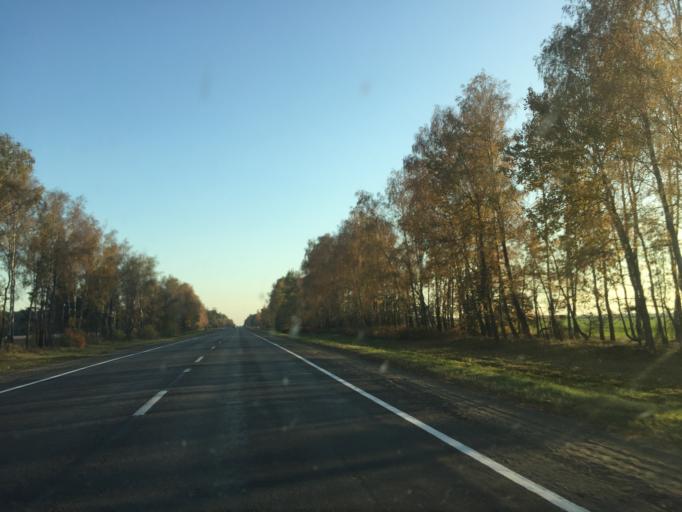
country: BY
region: Mogilev
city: Poselok Voskhod
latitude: 53.7370
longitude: 30.3663
